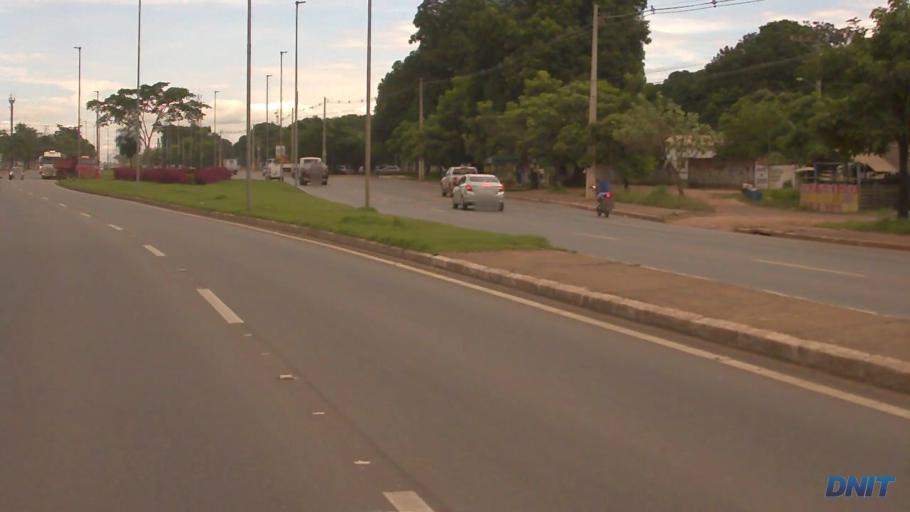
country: BR
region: Mato Grosso
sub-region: Cuiaba
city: Cuiaba
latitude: -15.6446
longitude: -56.0126
